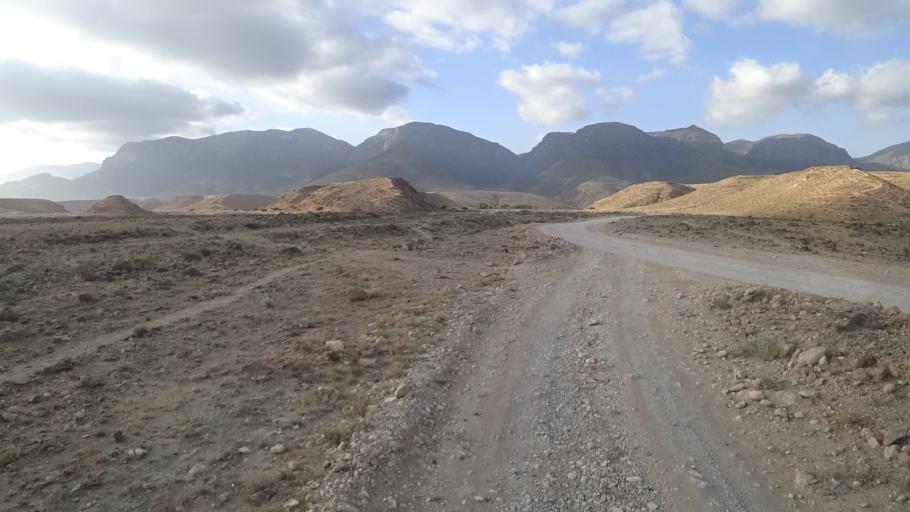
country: OM
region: Zufar
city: Salalah
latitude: 16.9786
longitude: 53.8531
